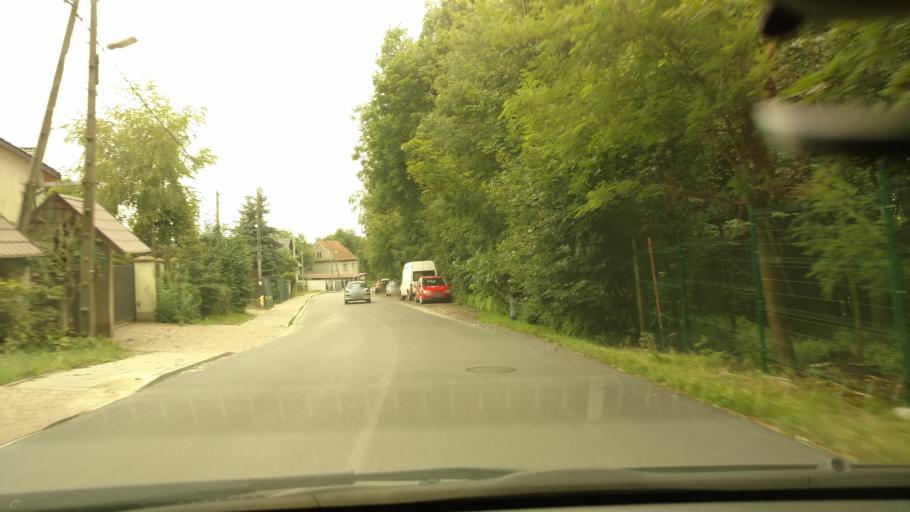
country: PL
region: Lesser Poland Voivodeship
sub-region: Powiat krakowski
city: Zielonki
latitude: 50.1105
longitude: 19.9430
